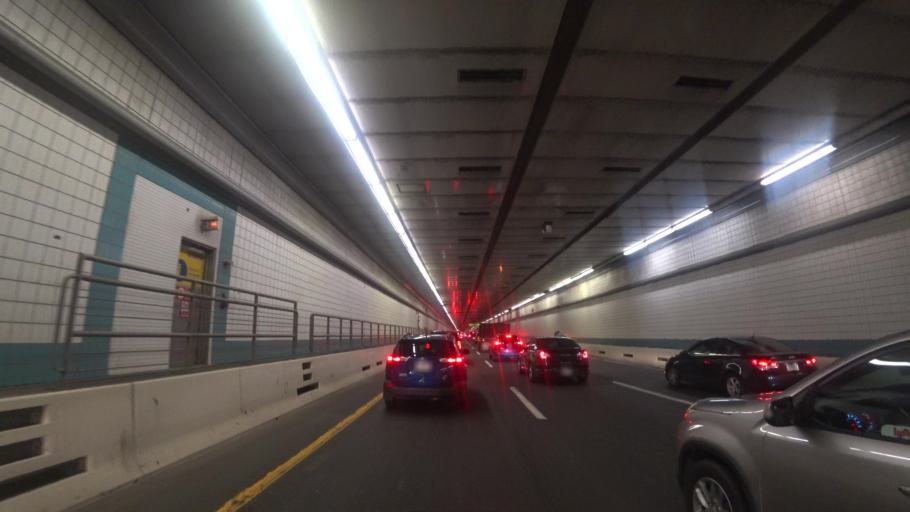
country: US
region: Massachusetts
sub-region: Suffolk County
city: Boston
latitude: 42.3605
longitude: -71.0283
